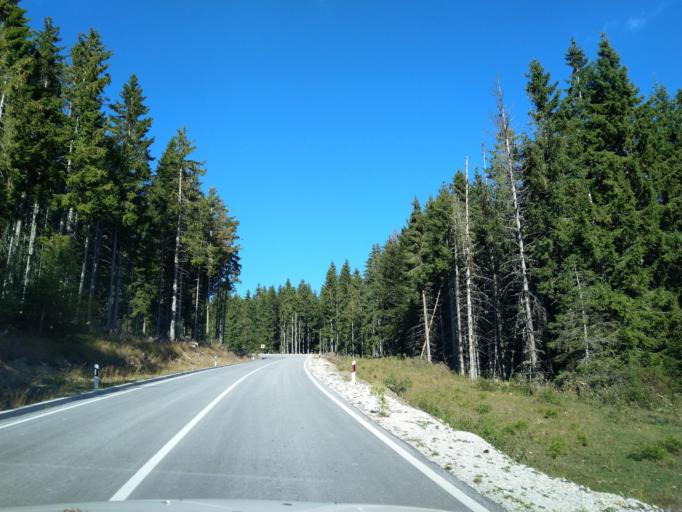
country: RS
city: Sokolovica
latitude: 43.3013
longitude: 20.3080
